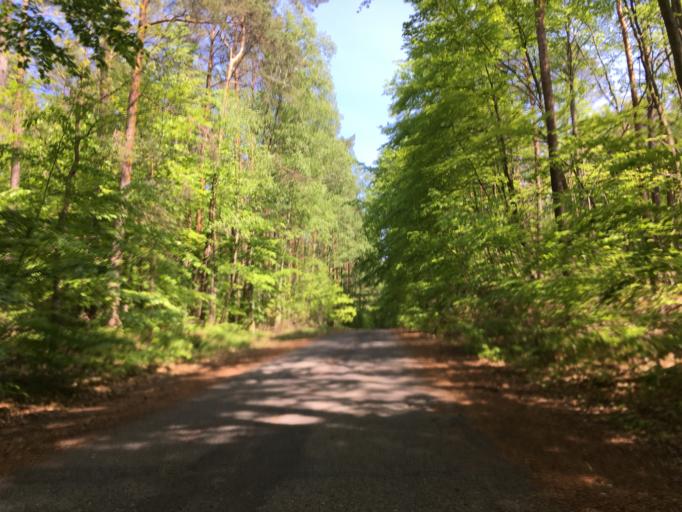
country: DE
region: Brandenburg
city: Wandlitz
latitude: 52.7357
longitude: 13.4758
